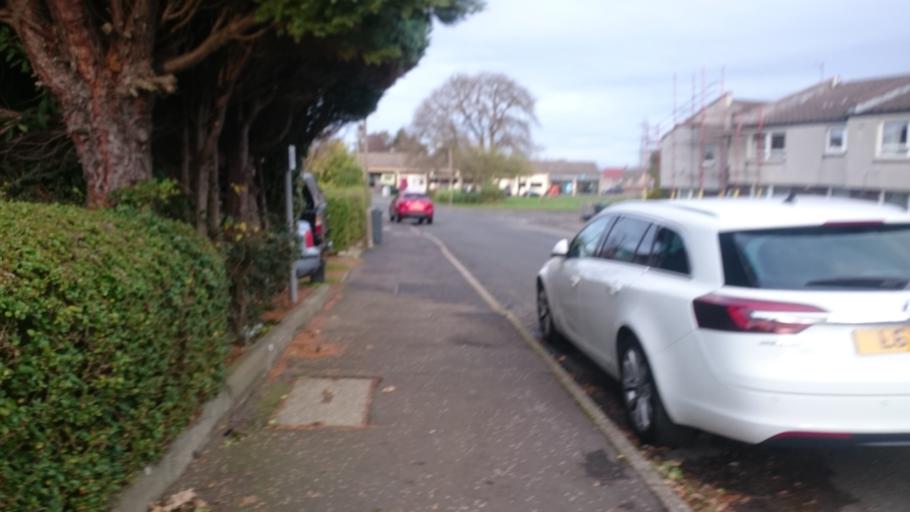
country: GB
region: Scotland
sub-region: Edinburgh
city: Currie
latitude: 55.8994
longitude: -3.3061
